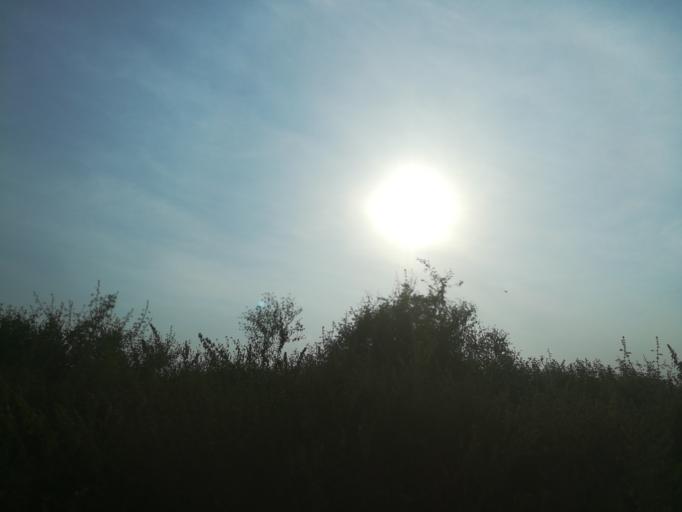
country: NG
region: Abuja Federal Capital Territory
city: Abuja
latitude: 9.0918
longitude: 7.3705
